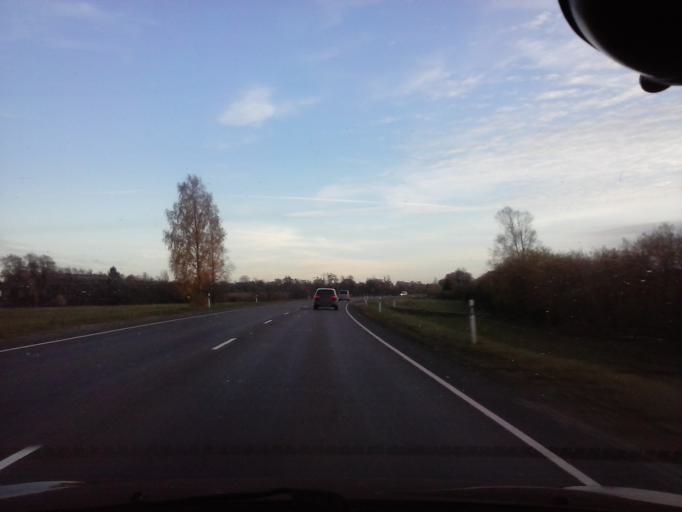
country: EE
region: Harju
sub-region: Nissi vald
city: Turba
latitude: 58.9235
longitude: 24.1117
